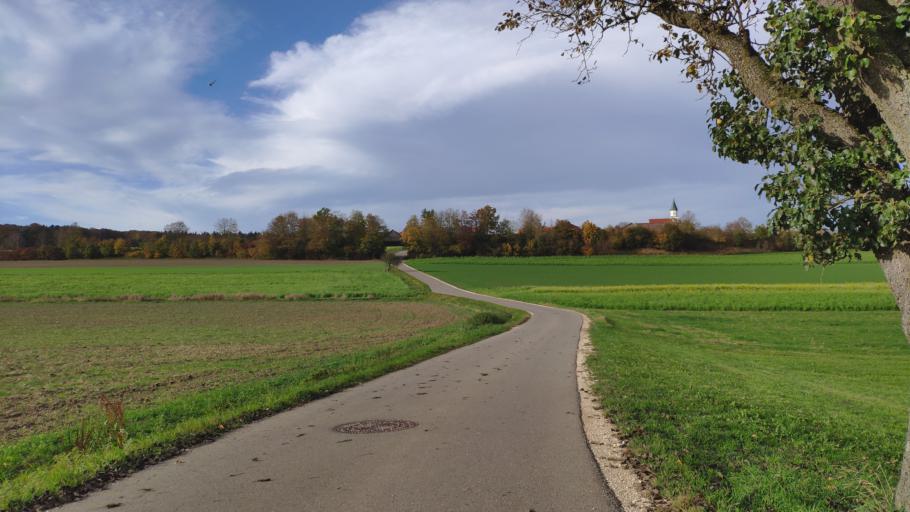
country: DE
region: Baden-Wuerttemberg
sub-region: Tuebingen Region
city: Erbach
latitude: 48.3863
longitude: 9.9152
